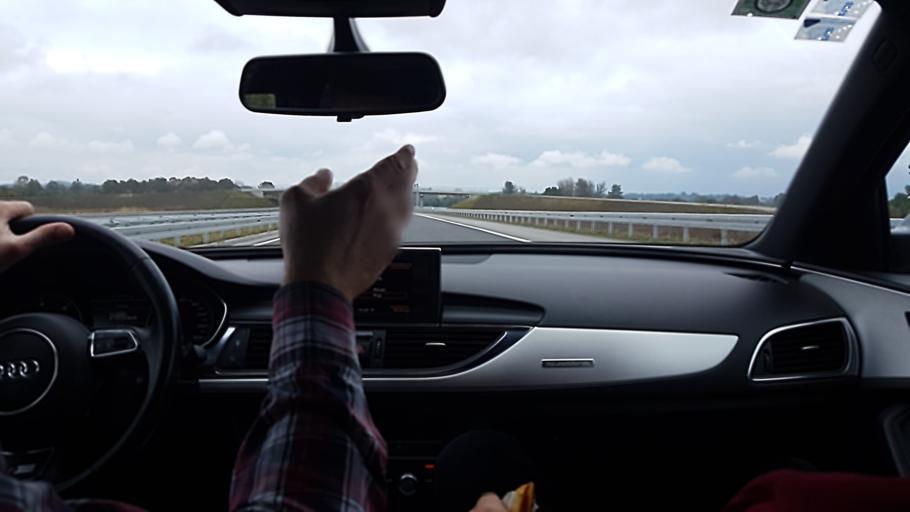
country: BA
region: Republika Srpska
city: Stanari
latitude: 44.8433
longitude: 17.7879
